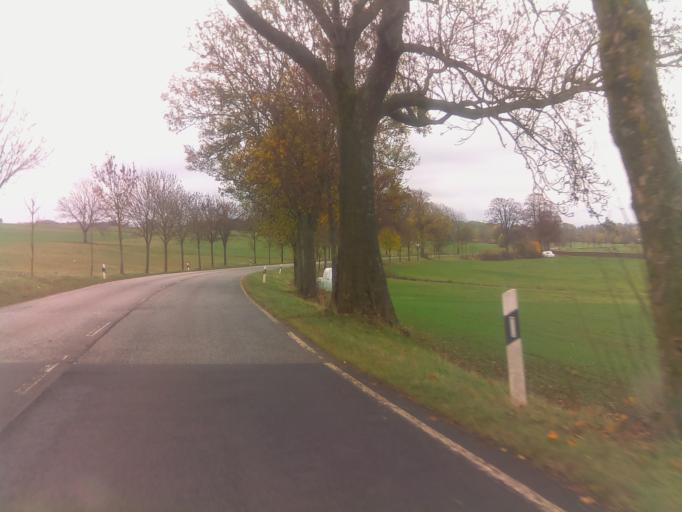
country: DE
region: Hesse
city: Herbstein
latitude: 50.5383
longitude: 9.3656
